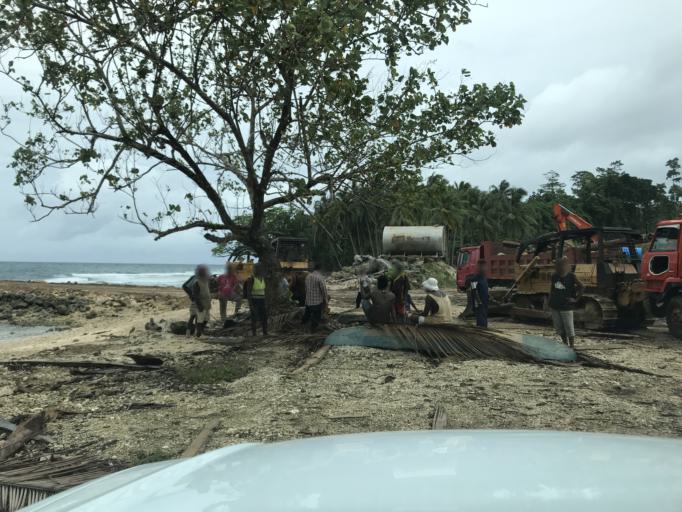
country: SB
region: Malaita
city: Auki
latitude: -8.6321
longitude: 160.6597
